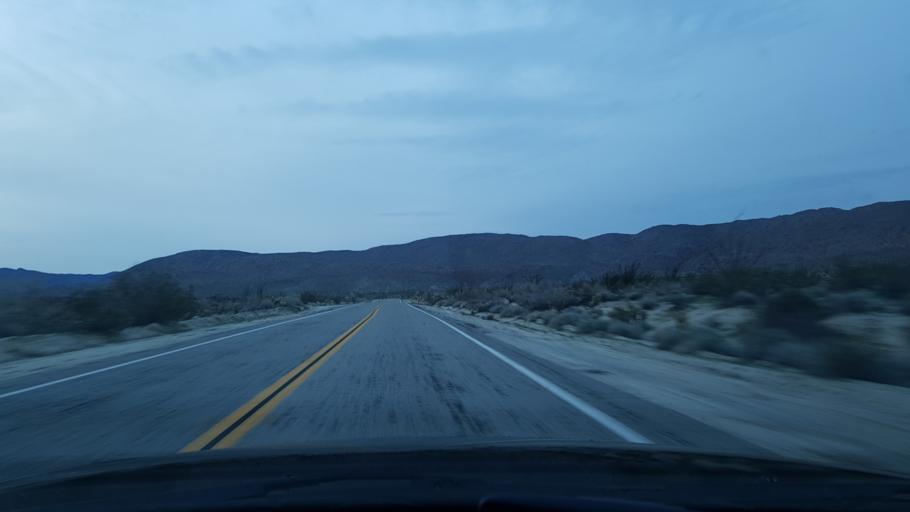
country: US
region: California
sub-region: San Diego County
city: Pine Valley
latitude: 32.9709
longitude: -116.3393
